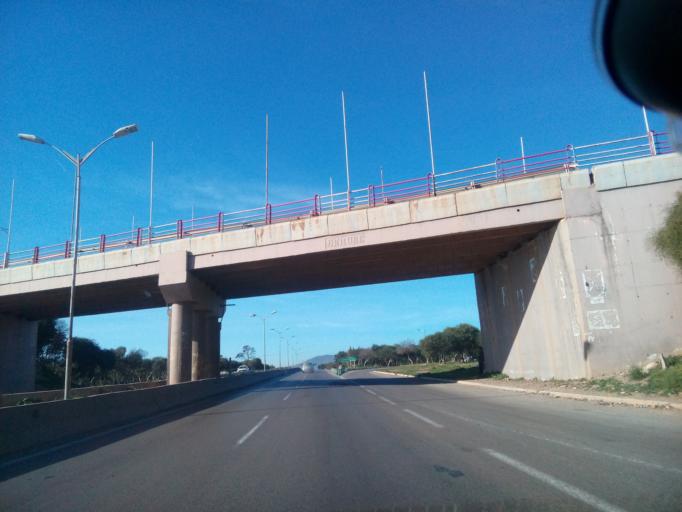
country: DZ
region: Oran
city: Ain el Bya
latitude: 35.7958
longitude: -0.3824
